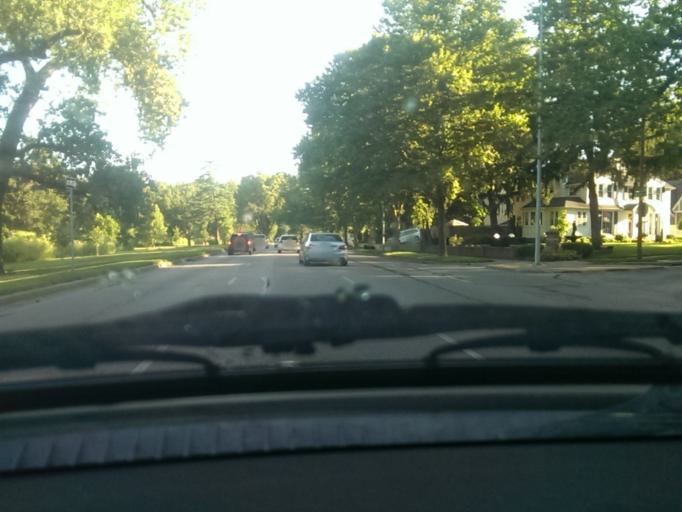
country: US
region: Kansas
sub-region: Johnson County
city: Westwood
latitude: 39.0366
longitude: -94.6016
